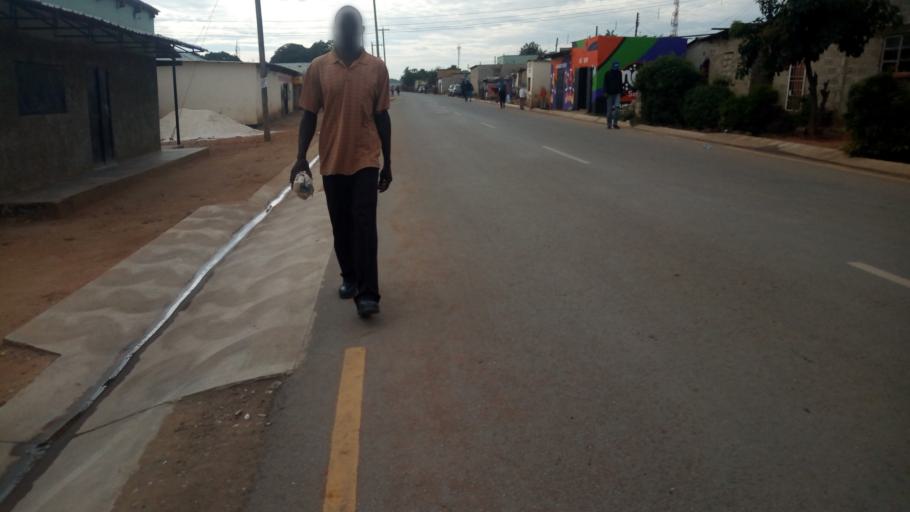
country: ZM
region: Lusaka
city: Lusaka
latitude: -15.3963
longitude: 28.2872
